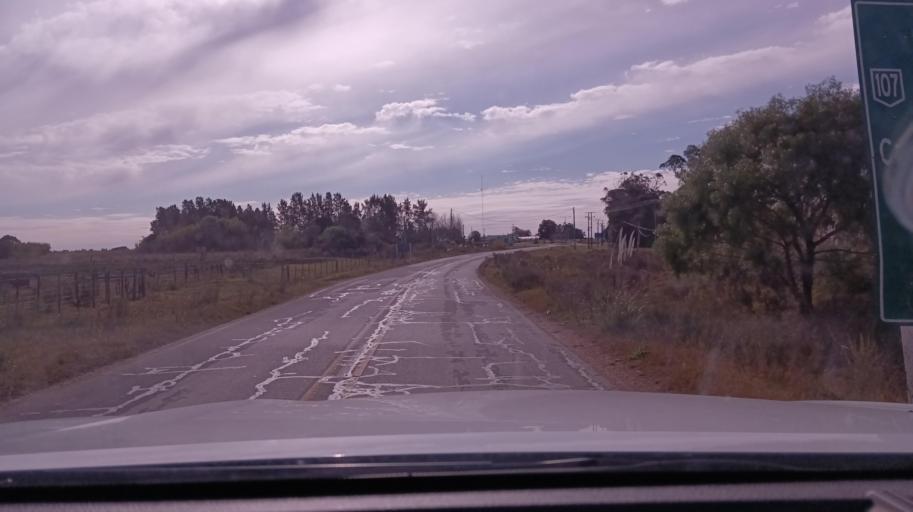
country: UY
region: Canelones
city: Sauce
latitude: -34.6270
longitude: -56.1114
